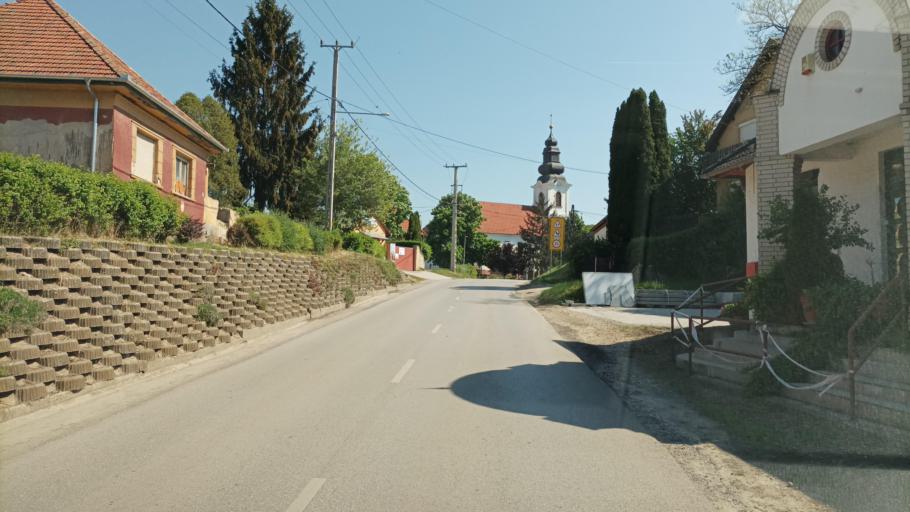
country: HU
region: Pest
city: Gomba
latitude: 47.3699
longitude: 19.5302
